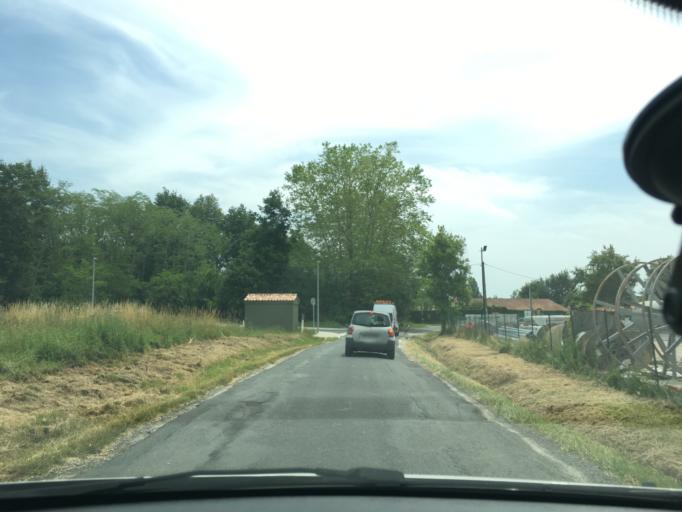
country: FR
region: Aquitaine
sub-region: Departement de la Gironde
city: Castelnau-de-Medoc
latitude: 45.0370
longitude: -0.8027
